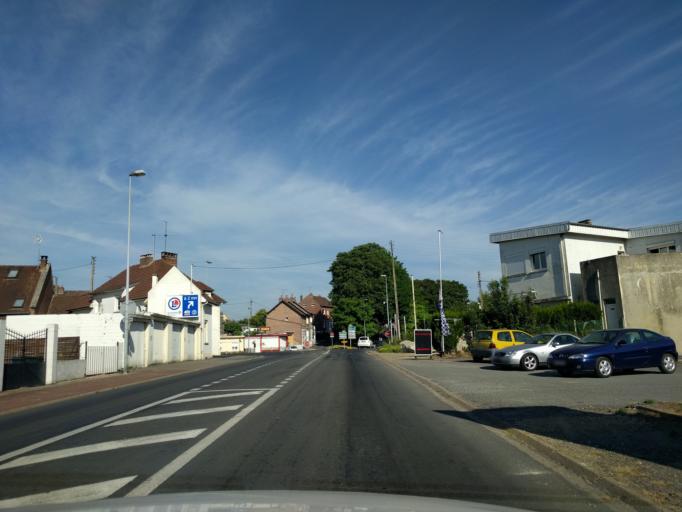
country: FR
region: Picardie
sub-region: Departement de l'Oise
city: Breteuil
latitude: 49.6294
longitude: 2.2949
